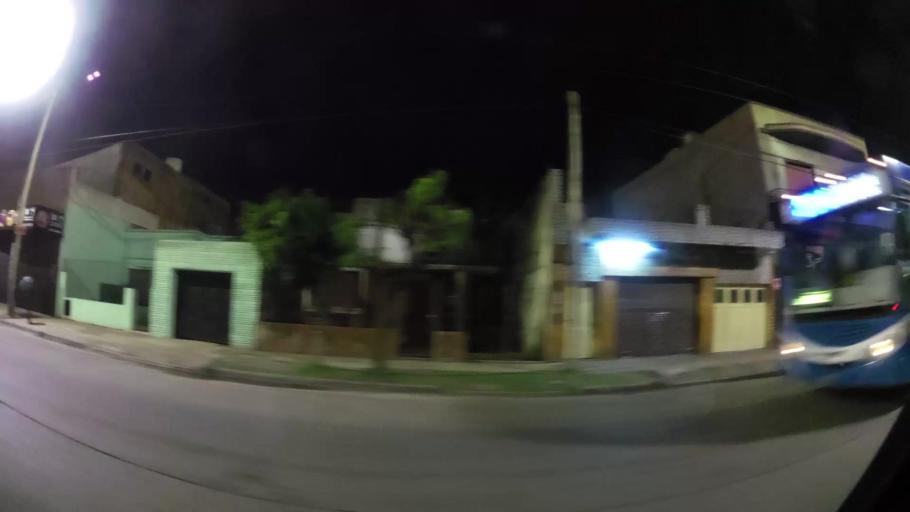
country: AR
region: Buenos Aires
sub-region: Partido de Lanus
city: Lanus
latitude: -34.7200
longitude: -58.3601
